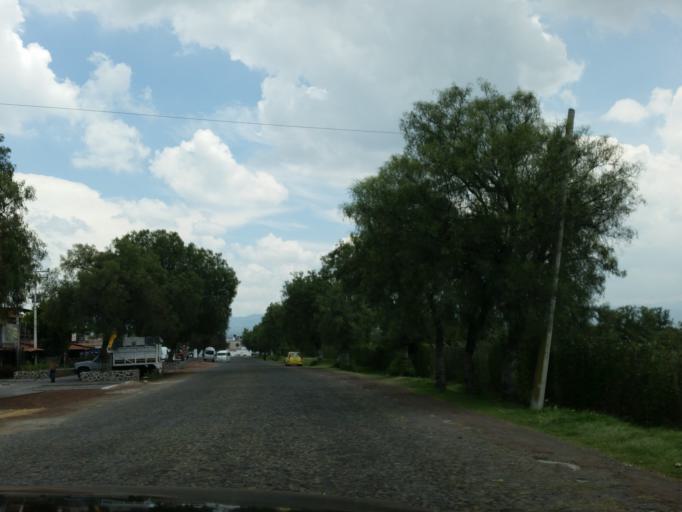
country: MX
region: Morelos
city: San Martin de las Piramides
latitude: 19.6996
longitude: -98.8405
